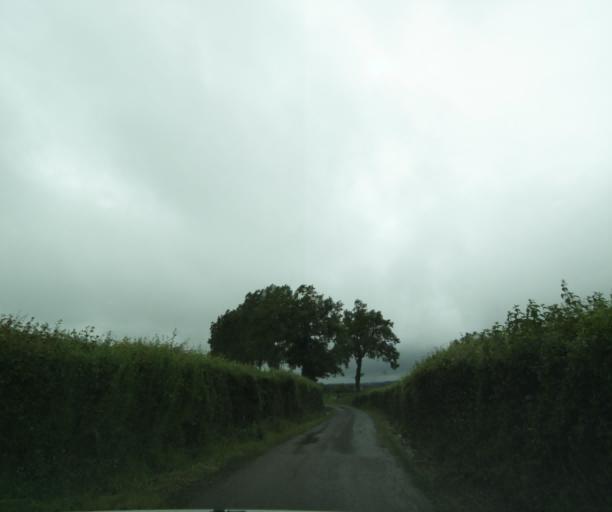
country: FR
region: Bourgogne
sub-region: Departement de Saone-et-Loire
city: Charolles
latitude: 46.3841
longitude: 4.2232
